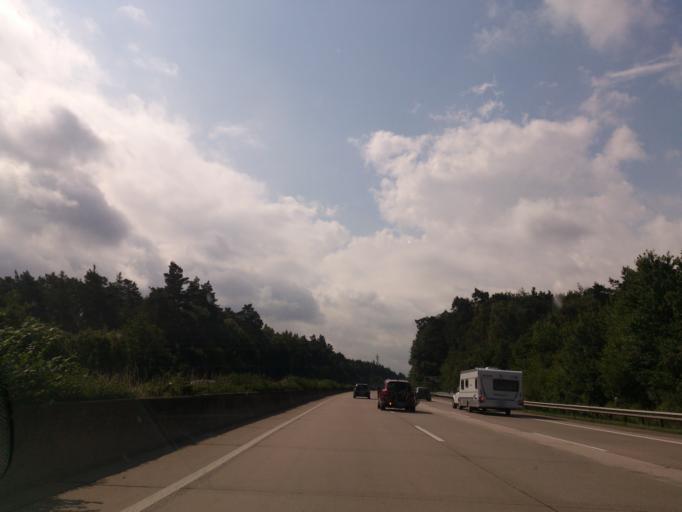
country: DE
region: Lower Saxony
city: Toppenstedt
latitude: 53.2612
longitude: 10.0879
